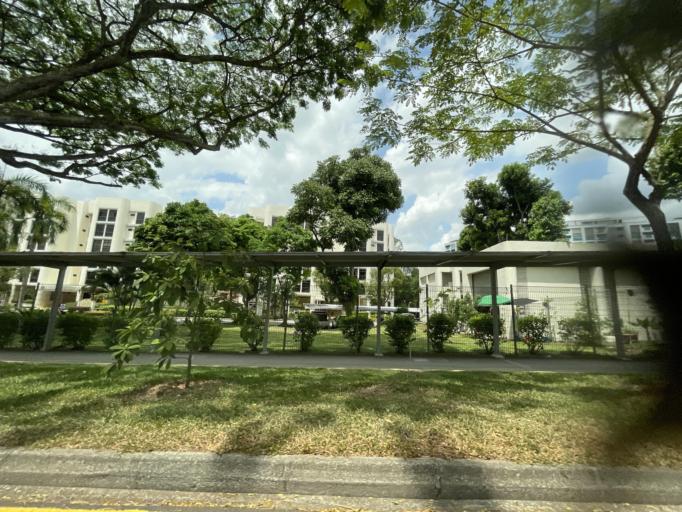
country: MY
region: Johor
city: Johor Bahru
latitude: 1.3727
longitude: 103.7686
